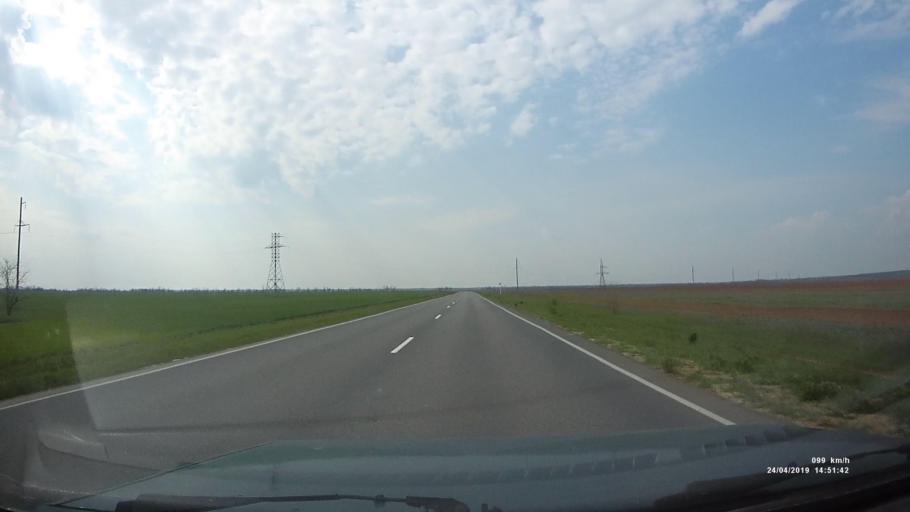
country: RU
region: Rostov
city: Remontnoye
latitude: 46.5268
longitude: 43.6958
